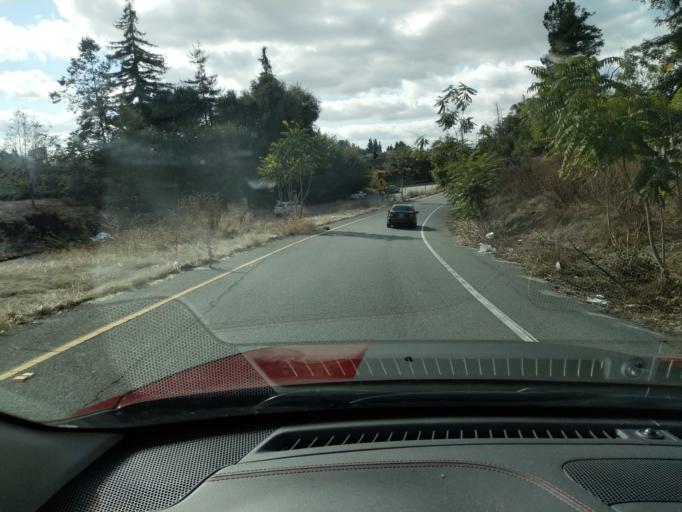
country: US
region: California
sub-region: Santa Clara County
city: San Jose
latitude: 37.3245
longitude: -121.8947
